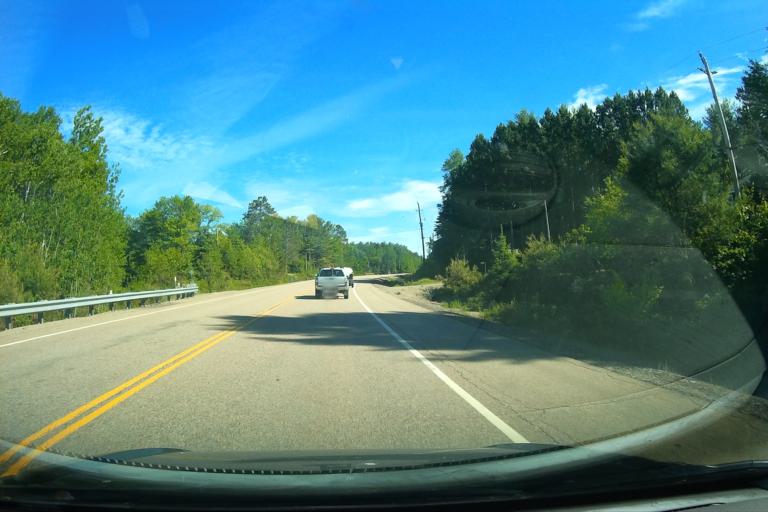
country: CA
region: Ontario
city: Deep River
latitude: 46.2077
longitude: -77.8855
